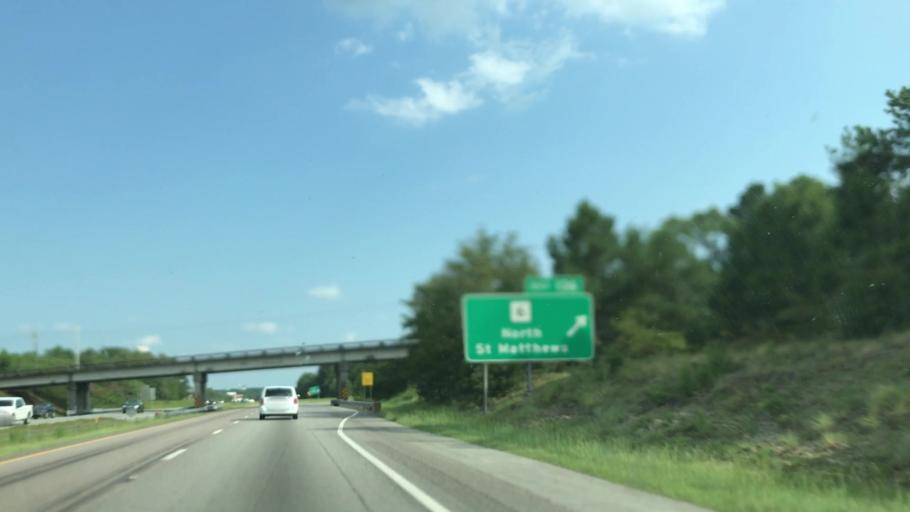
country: US
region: South Carolina
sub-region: Calhoun County
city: Saint Matthews
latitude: 33.6735
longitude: -80.8986
